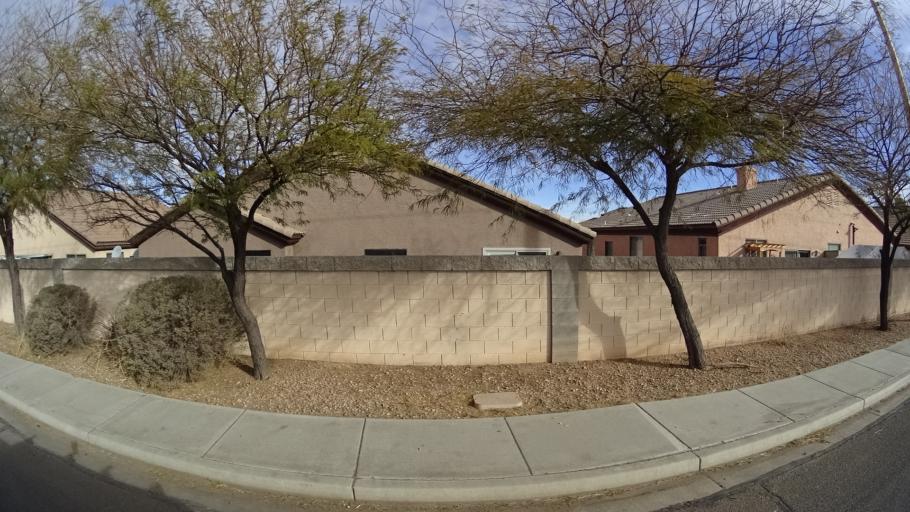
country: US
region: Arizona
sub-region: Mohave County
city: New Kingman-Butler
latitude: 35.2249
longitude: -113.9795
